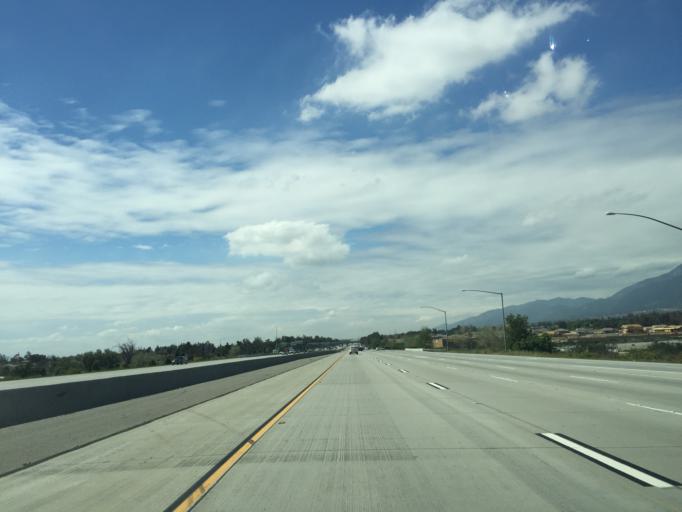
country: US
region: California
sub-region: San Bernardino County
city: Fontana
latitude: 34.1364
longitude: -117.5015
